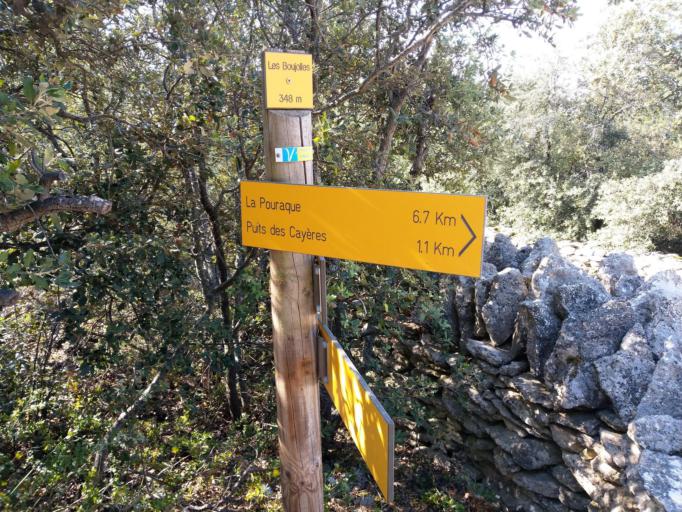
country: FR
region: Provence-Alpes-Cote d'Azur
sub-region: Departement du Vaucluse
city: Gordes
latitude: 43.9127
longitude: 5.1696
